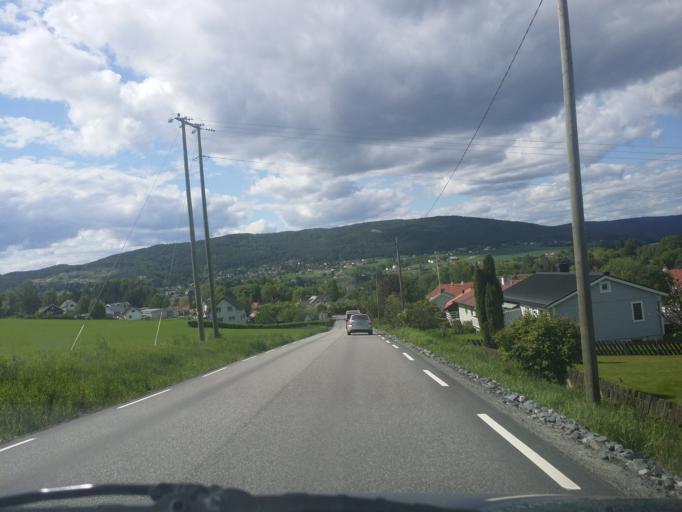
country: NO
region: Oppland
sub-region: Jevnaker
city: Jevnaker
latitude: 60.2364
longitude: 10.4062
